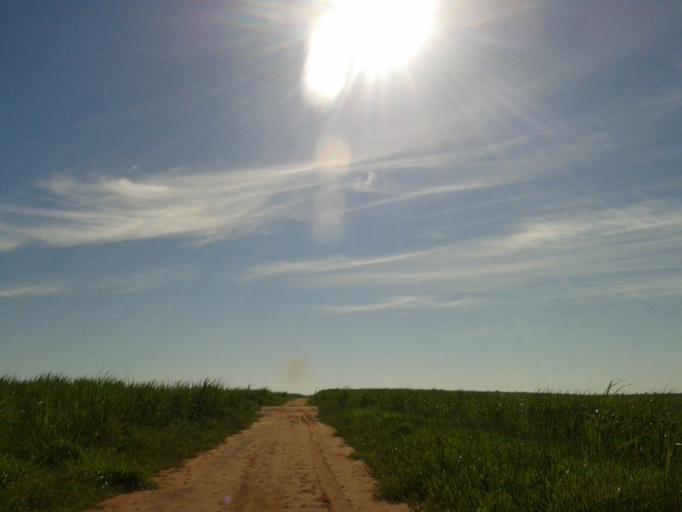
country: BR
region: Minas Gerais
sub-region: Santa Vitoria
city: Santa Vitoria
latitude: -19.1254
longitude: -50.0070
